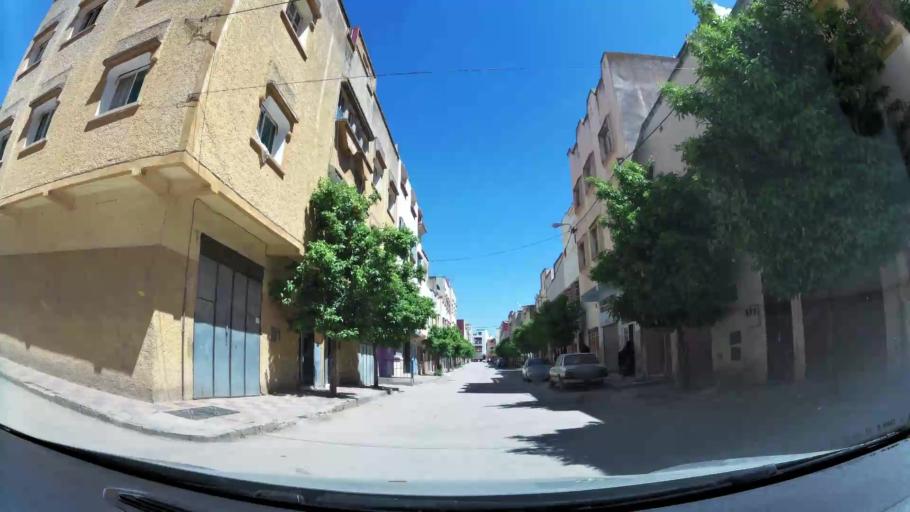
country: MA
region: Meknes-Tafilalet
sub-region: Meknes
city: Meknes
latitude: 33.8733
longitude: -5.5640
